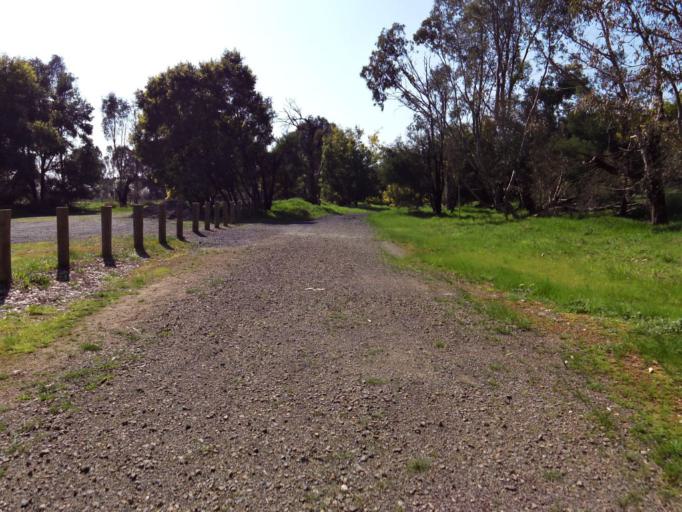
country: AU
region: Victoria
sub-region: Murrindindi
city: Alexandra
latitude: -37.1502
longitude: 145.5834
